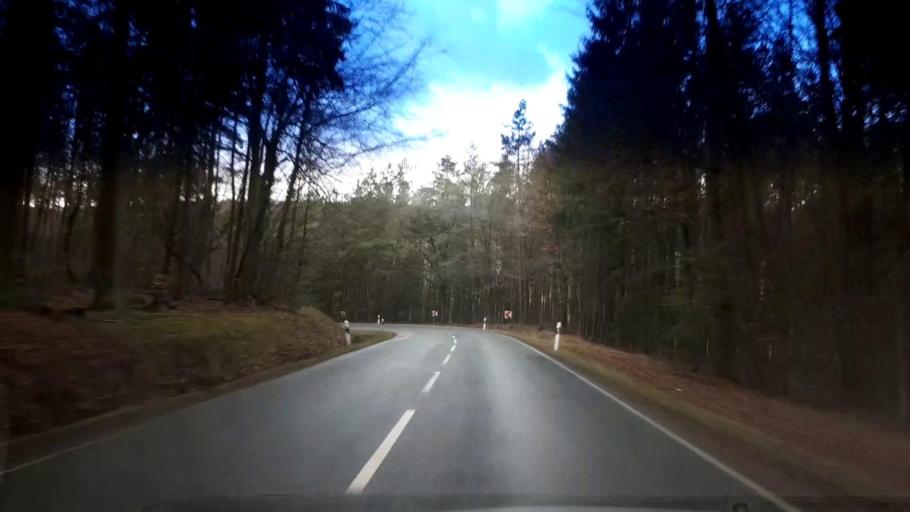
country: DE
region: Bavaria
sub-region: Upper Franconia
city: Lauter
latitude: 49.9671
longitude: 10.7594
